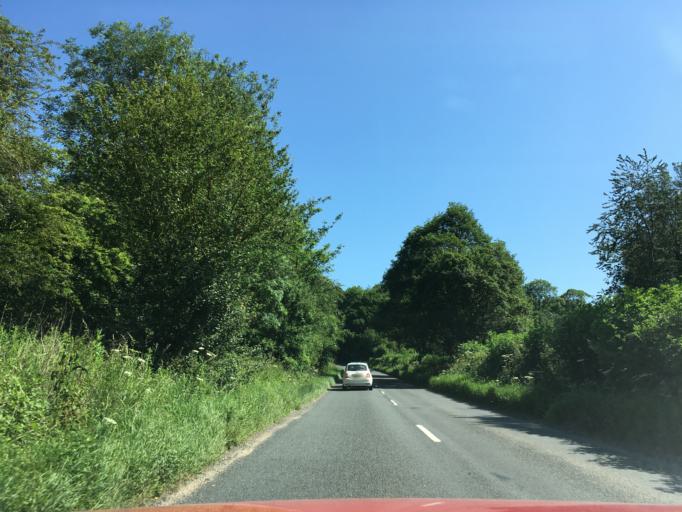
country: GB
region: England
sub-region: Gloucestershire
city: Westfield
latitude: 51.9064
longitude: -1.8098
